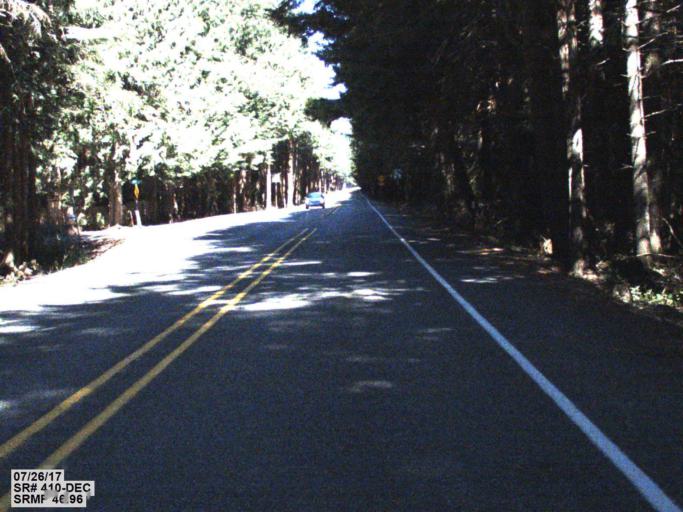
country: US
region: Washington
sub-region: King County
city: Riverbend
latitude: 47.1125
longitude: -121.6021
